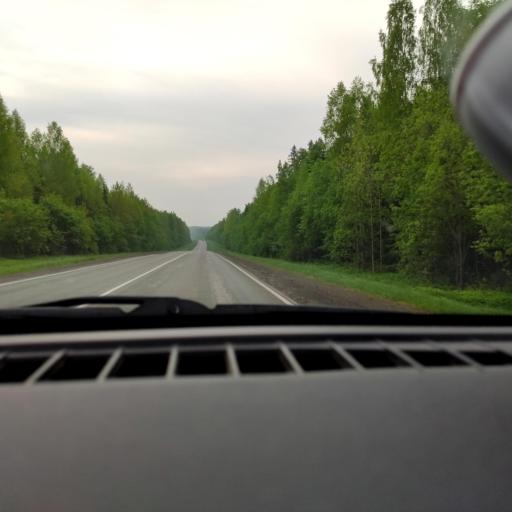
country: RU
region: Perm
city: Perm
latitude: 58.1742
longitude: 56.2314
